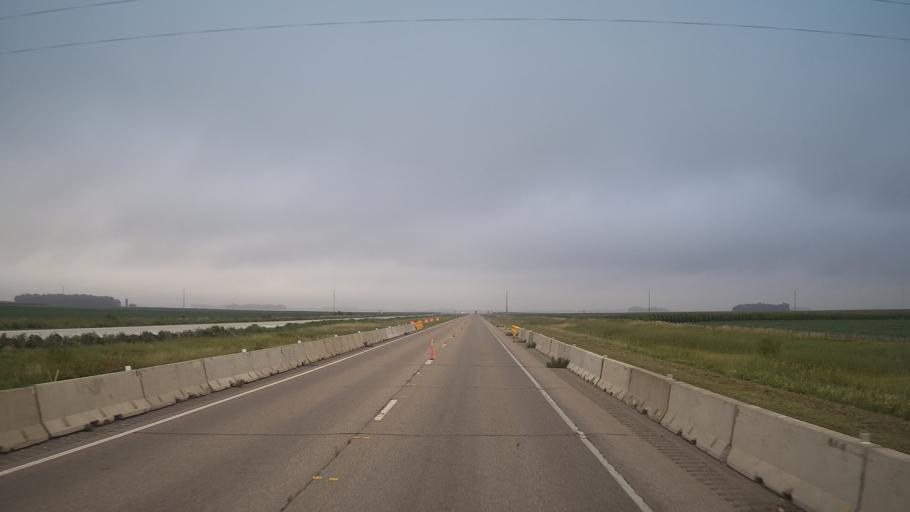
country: US
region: Minnesota
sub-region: Faribault County
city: Blue Earth
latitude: 43.6664
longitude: -94.1773
